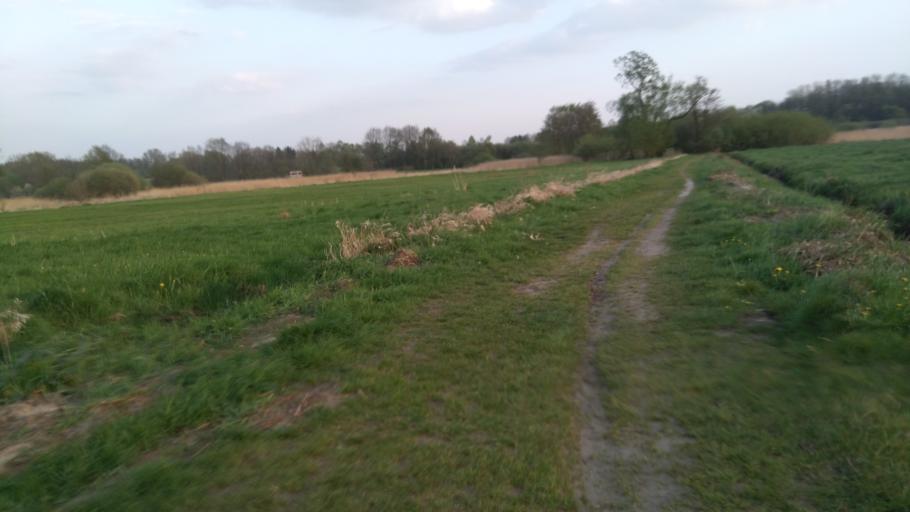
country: DE
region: Lower Saxony
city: Bliedersdorf
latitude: 53.4921
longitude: 9.5555
